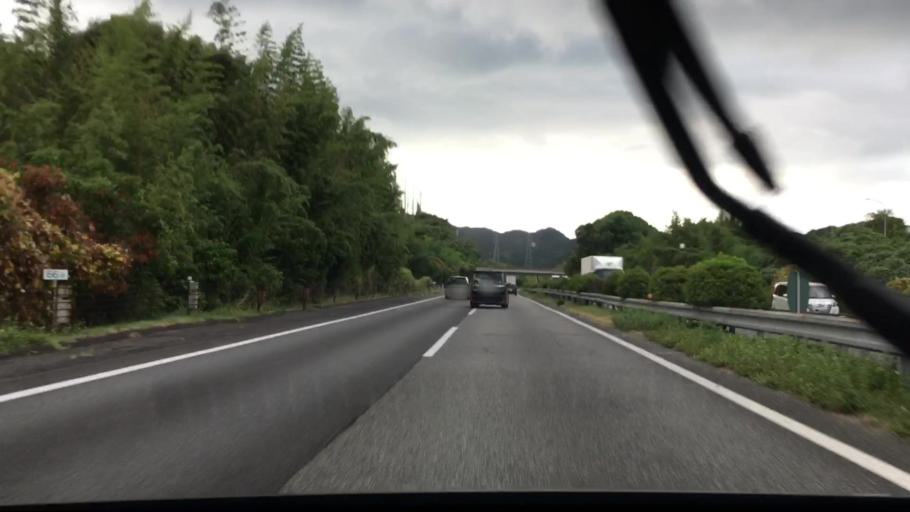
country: JP
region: Fukuoka
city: Sasaguri
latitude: 33.6413
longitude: 130.4870
